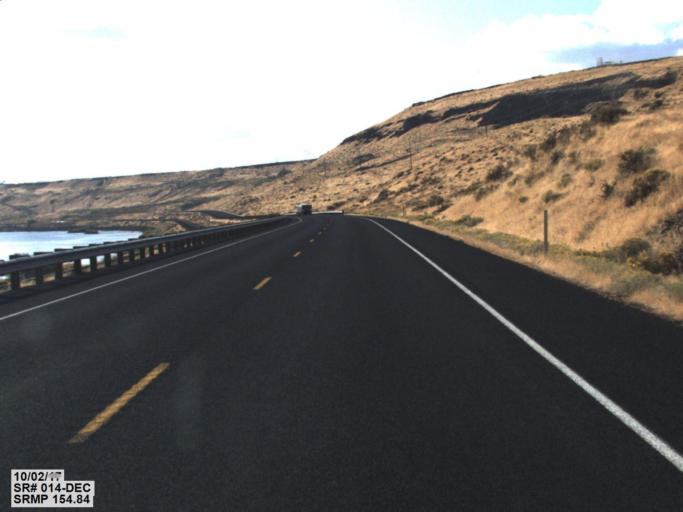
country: US
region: Oregon
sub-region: Morrow County
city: Boardman
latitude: 45.8699
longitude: -119.8302
